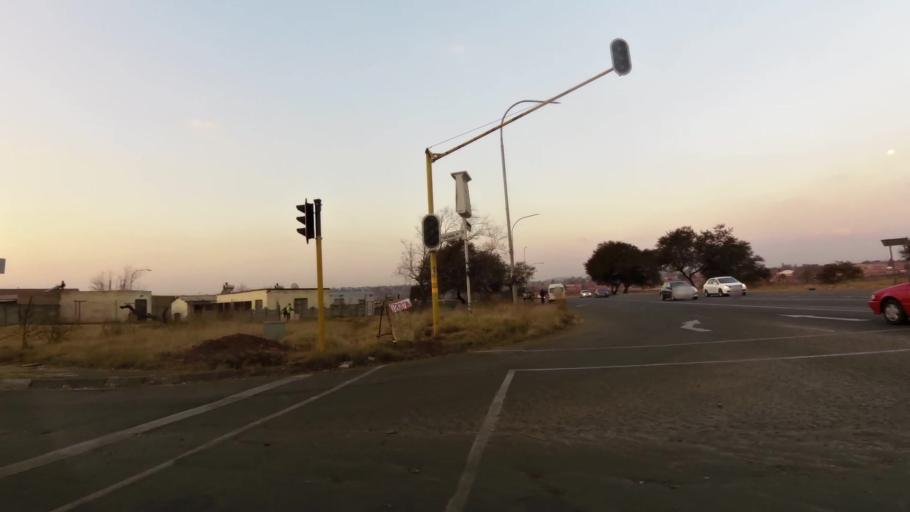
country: ZA
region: Gauteng
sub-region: City of Johannesburg Metropolitan Municipality
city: Soweto
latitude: -26.2917
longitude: 27.8807
